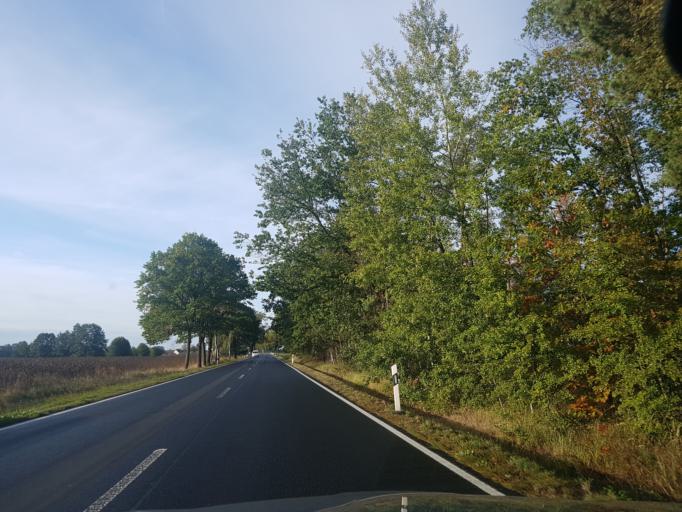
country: DE
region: Brandenburg
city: Herzberg
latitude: 51.6250
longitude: 13.1518
